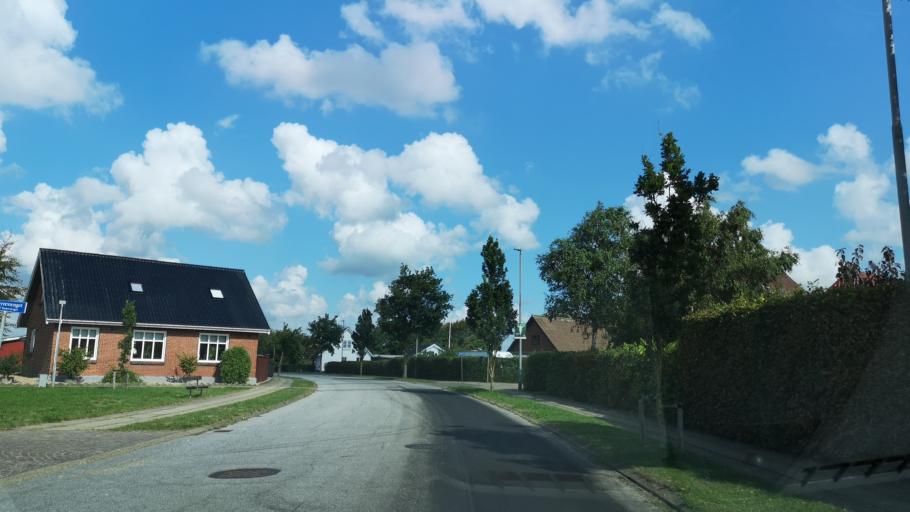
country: DK
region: Central Jutland
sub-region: Ringkobing-Skjern Kommune
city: Skjern
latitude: 55.9474
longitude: 8.4872
